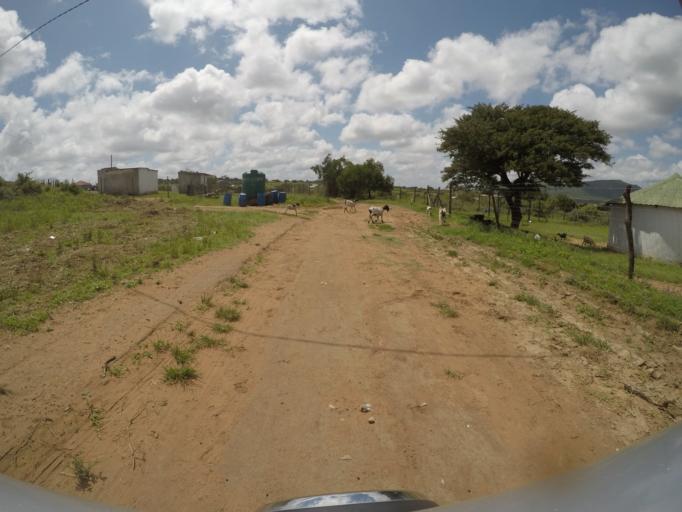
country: ZA
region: KwaZulu-Natal
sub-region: uThungulu District Municipality
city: Empangeni
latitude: -28.5867
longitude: 31.8414
